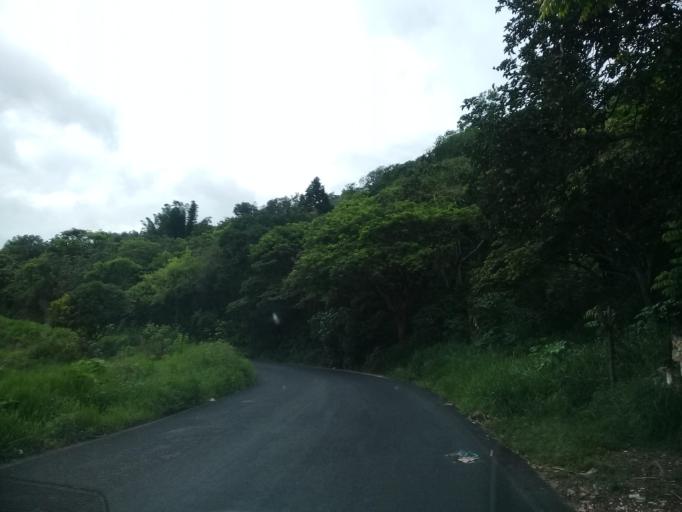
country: MX
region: Veracruz
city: El Castillo
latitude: 19.5609
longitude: -96.8428
